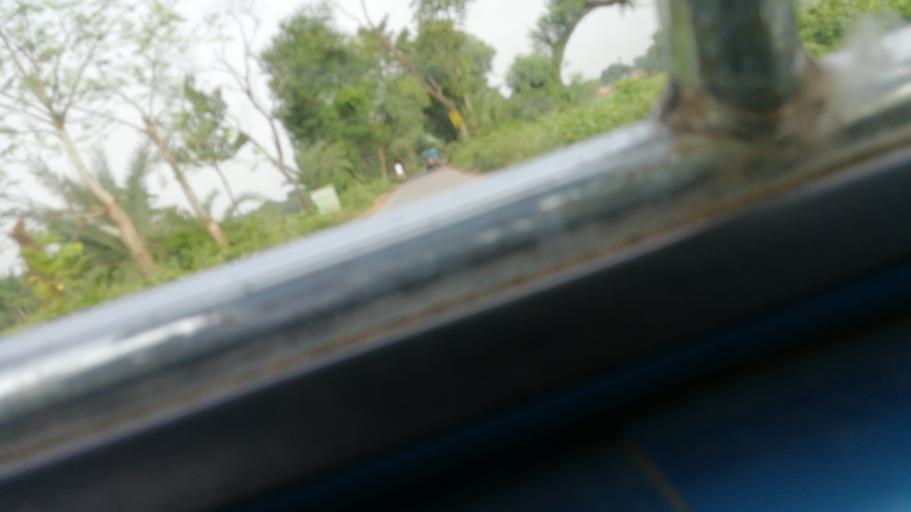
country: BD
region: Khulna
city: Kesabpur
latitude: 23.0257
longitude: 89.2546
